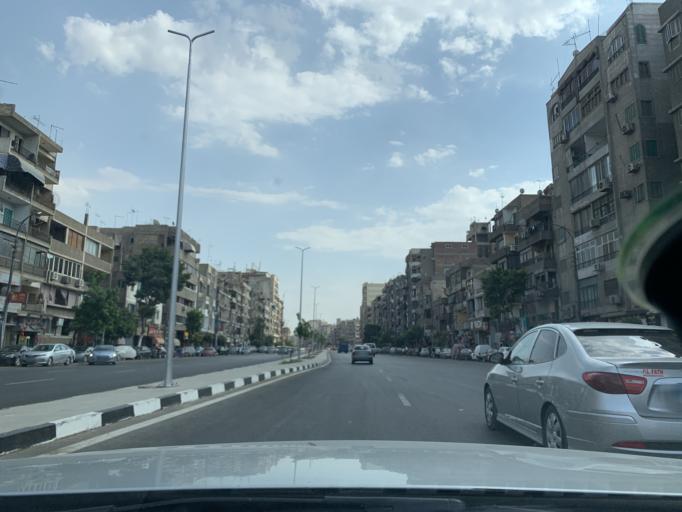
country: EG
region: Muhafazat al Qalyubiyah
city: Al Khankah
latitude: 30.1090
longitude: 31.3449
